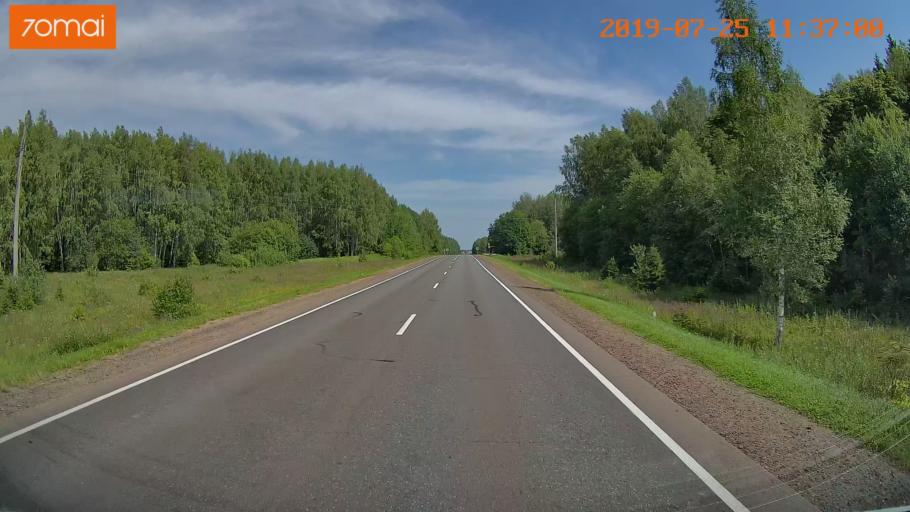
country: RU
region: Ivanovo
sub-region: Privolzhskiy Rayon
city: Ples
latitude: 57.4289
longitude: 41.4600
